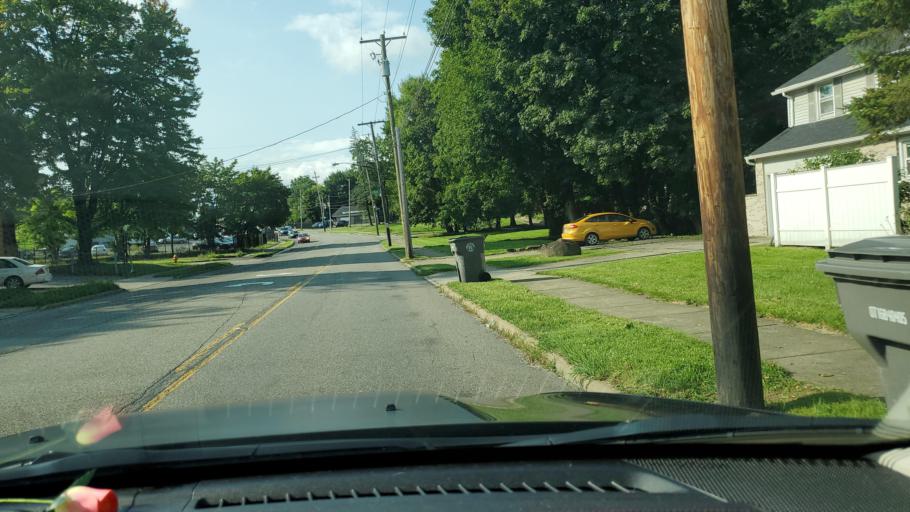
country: US
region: Ohio
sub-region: Mahoning County
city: Youngstown
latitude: 41.0831
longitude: -80.6751
